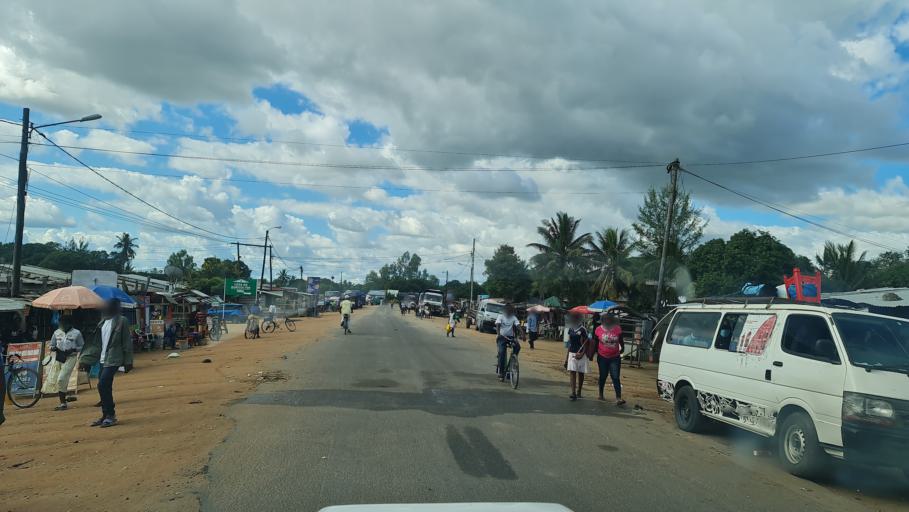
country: MZ
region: Zambezia
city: Quelimane
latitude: -17.5961
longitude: 36.8126
